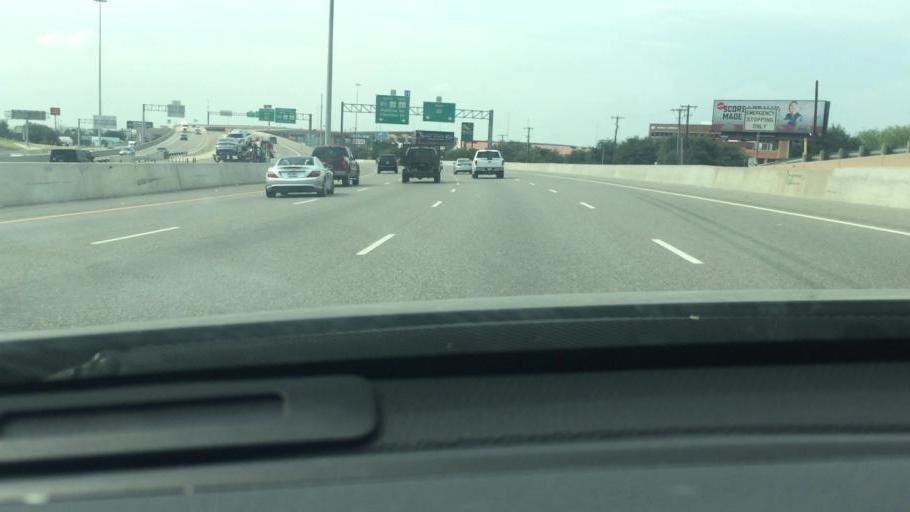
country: US
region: Texas
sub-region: Tarrant County
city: Hurst
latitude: 32.8382
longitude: -97.1939
